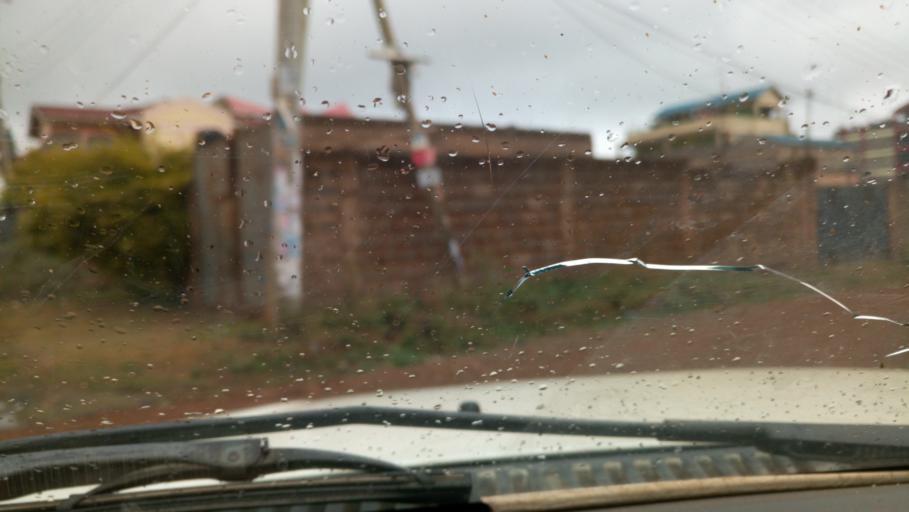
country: KE
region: Kiambu
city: Kiambu
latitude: -1.2102
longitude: 36.8858
